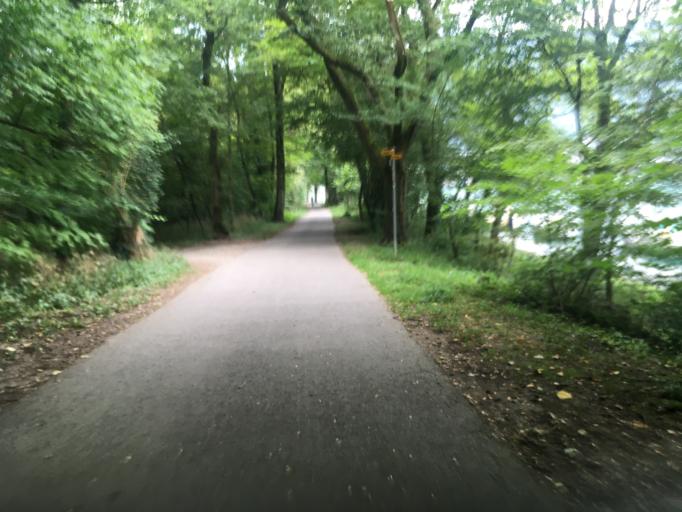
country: CH
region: Bern
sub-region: Biel/Bienne District
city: Nidau
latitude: 47.1234
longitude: 7.2307
